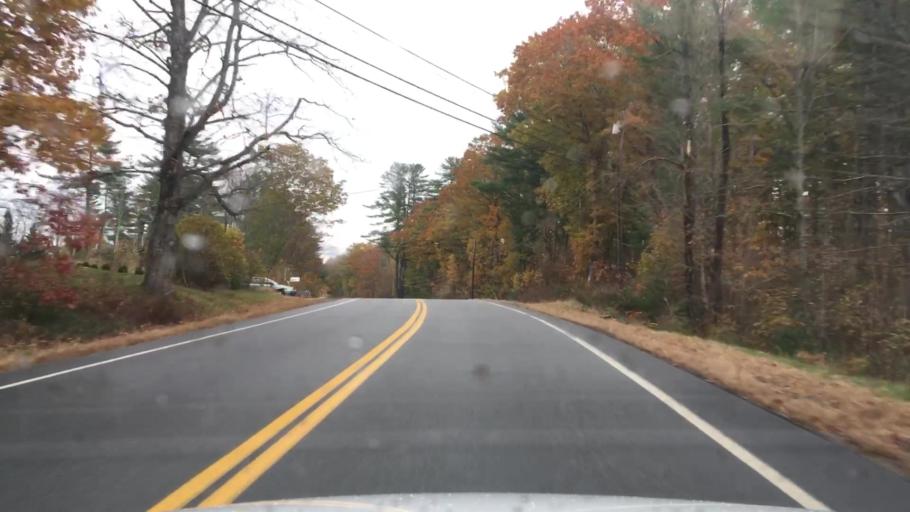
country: US
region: Maine
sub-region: Lincoln County
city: Jefferson
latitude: 44.2018
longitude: -69.4986
